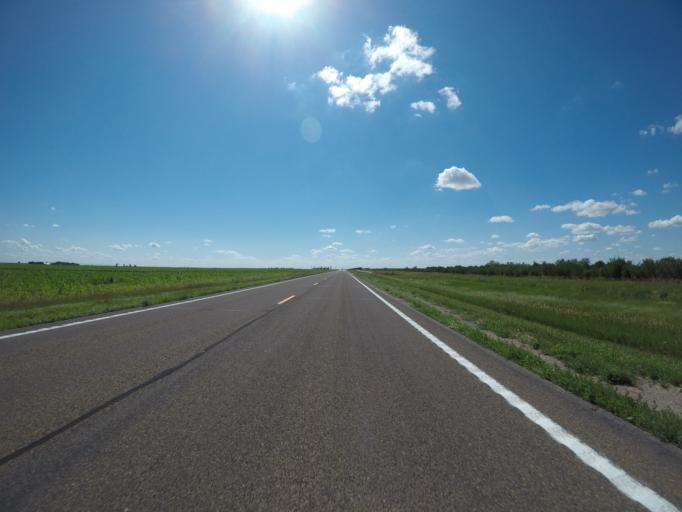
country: US
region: Nebraska
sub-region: Chase County
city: Imperial
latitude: 40.5377
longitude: -101.8857
